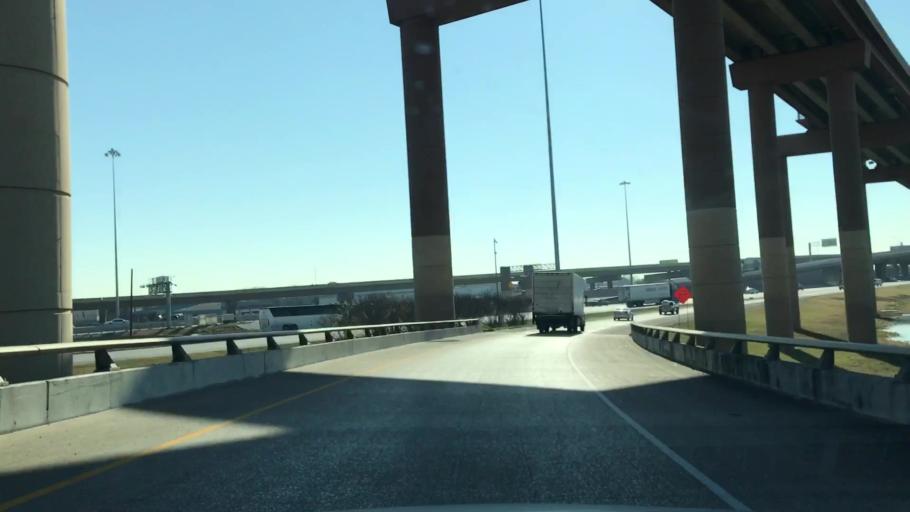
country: US
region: Texas
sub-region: Dallas County
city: Farmers Branch
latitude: 32.9064
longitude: -96.8989
